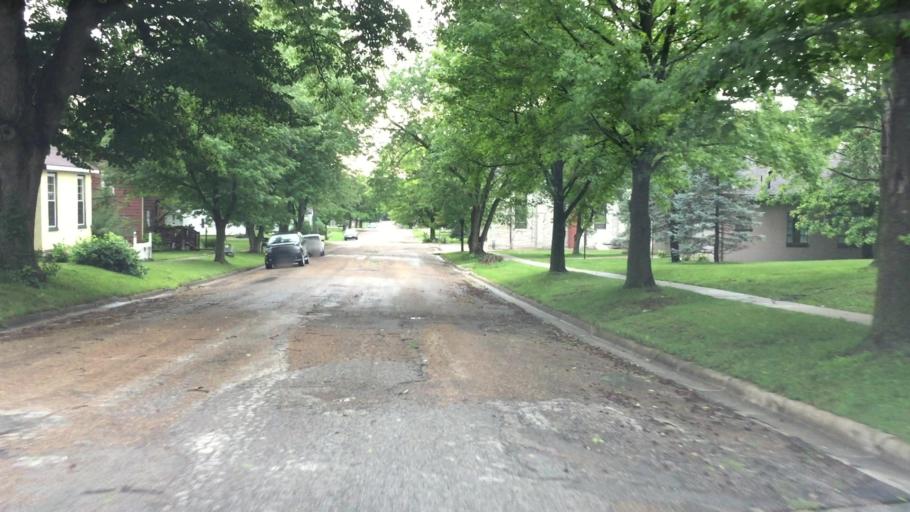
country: US
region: Illinois
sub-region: Hancock County
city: Warsaw
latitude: 40.3565
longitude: -91.4317
